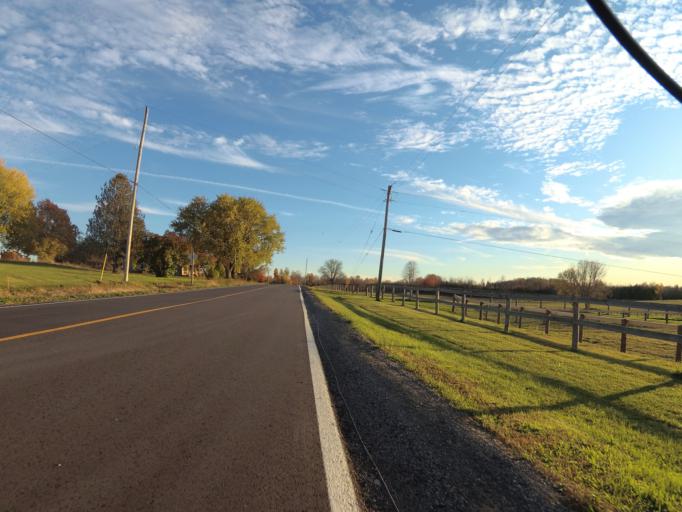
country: CA
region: Ontario
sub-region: Lanark County
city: Smiths Falls
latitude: 44.9544
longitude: -75.8141
